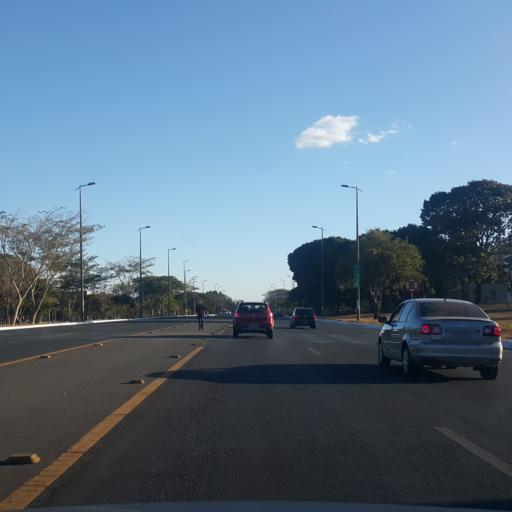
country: BR
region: Federal District
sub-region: Brasilia
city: Brasilia
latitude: -15.8056
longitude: -47.8889
